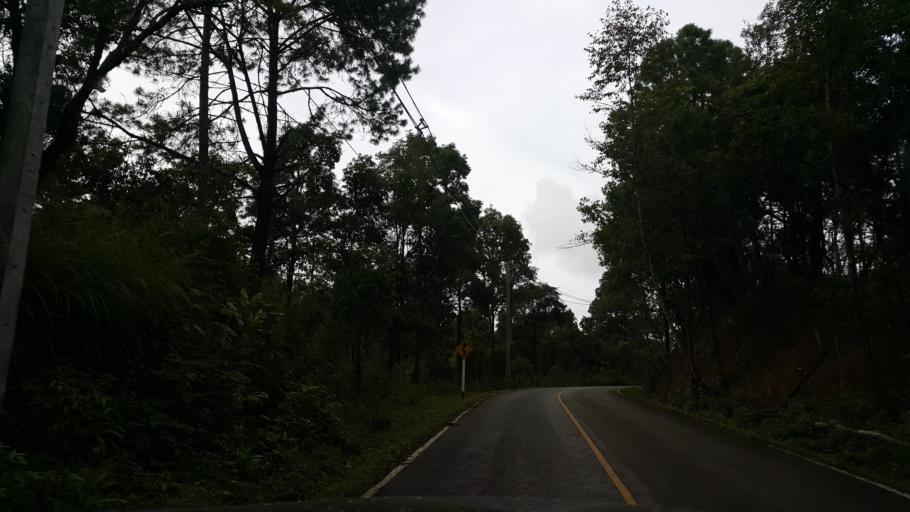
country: TH
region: Chiang Mai
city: Chaem Luang
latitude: 18.9174
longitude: 98.4807
